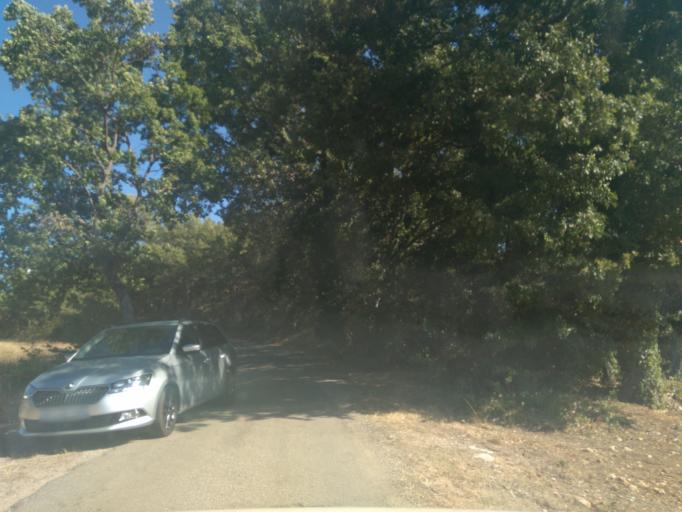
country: FR
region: Provence-Alpes-Cote d'Azur
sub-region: Departement du Var
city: Regusse
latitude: 43.6982
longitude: 6.1073
